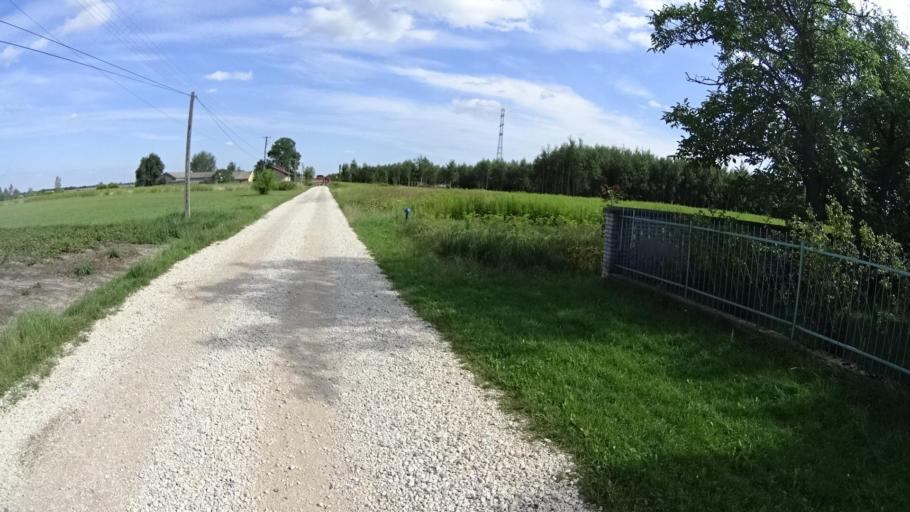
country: PL
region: Masovian Voivodeship
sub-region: Powiat piaseczynski
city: Lesznowola
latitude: 52.0657
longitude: 20.9395
